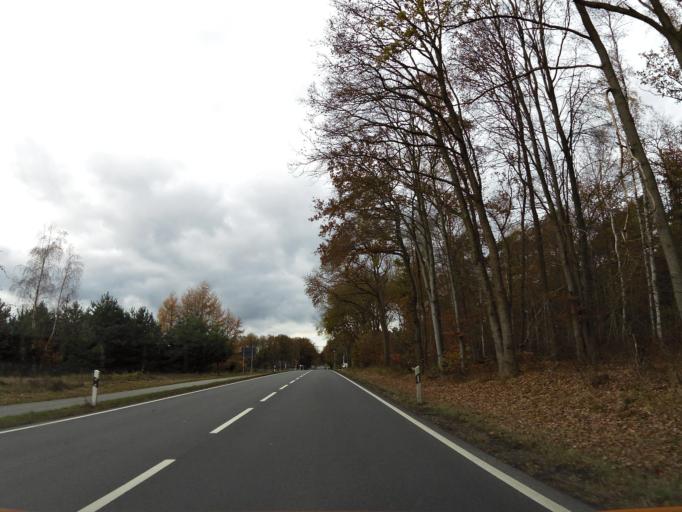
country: DE
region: Lower Saxony
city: Schnega
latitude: 52.9068
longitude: 10.9174
